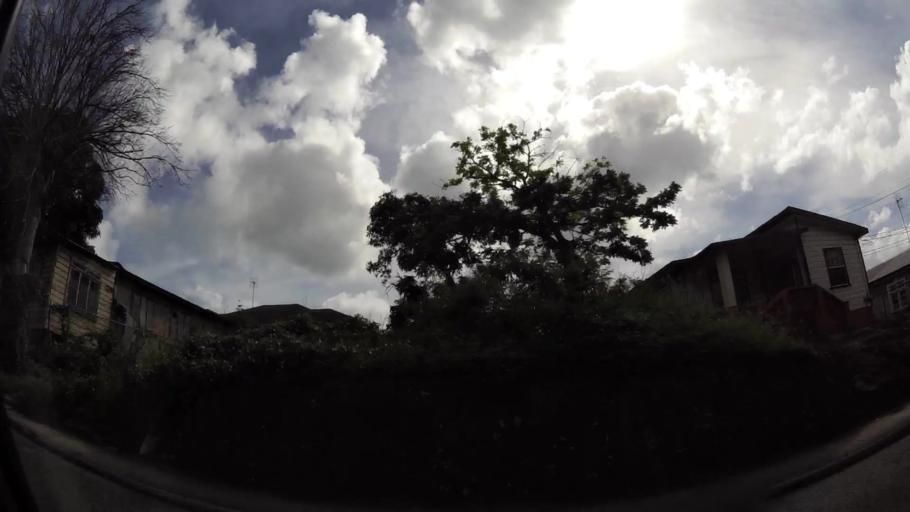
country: BB
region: Saint Michael
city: Bridgetown
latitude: 13.0937
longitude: -59.5963
